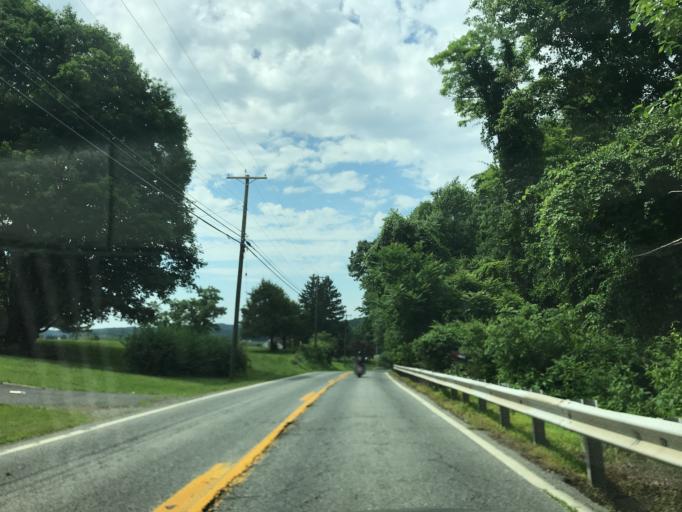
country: US
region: Maryland
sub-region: Harford County
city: Bel Air North
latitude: 39.6026
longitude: -76.3959
